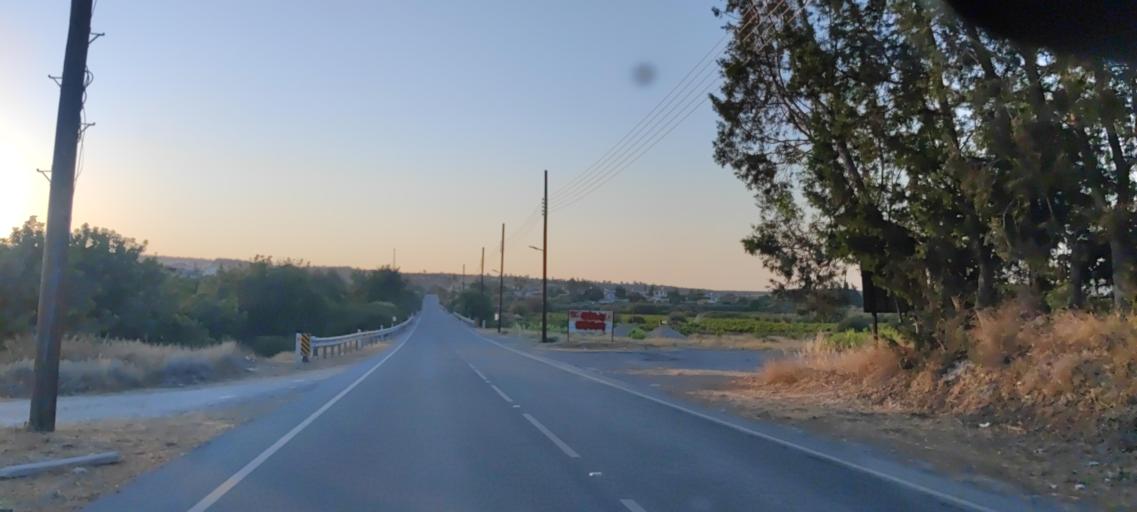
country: CY
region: Limassol
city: Sotira
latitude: 34.6776
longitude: 32.7858
